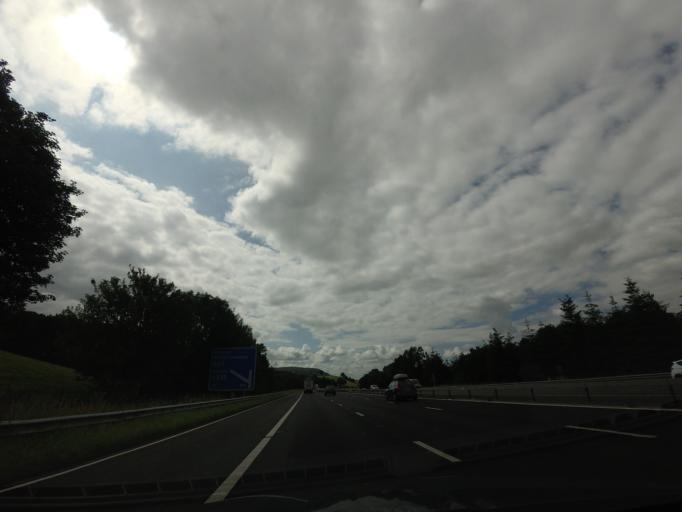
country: GB
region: England
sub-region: Cumbria
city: Milnthorpe
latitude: 54.2502
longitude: -2.6962
